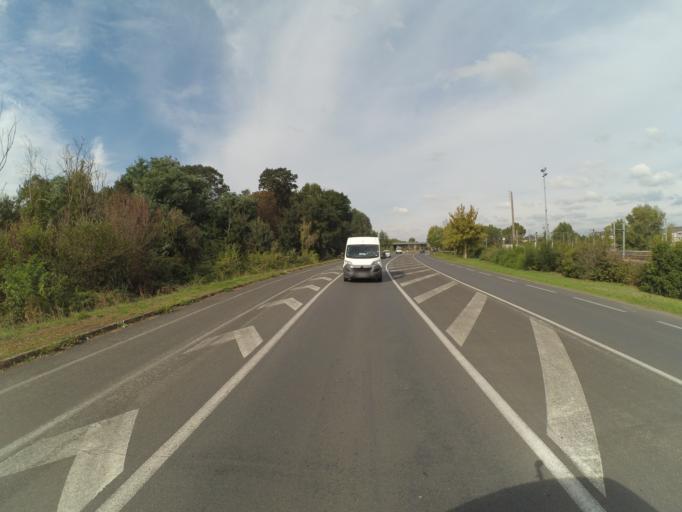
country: FR
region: Pays de la Loire
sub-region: Departement de Maine-et-Loire
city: Saumur
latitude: 47.2714
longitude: -0.0773
